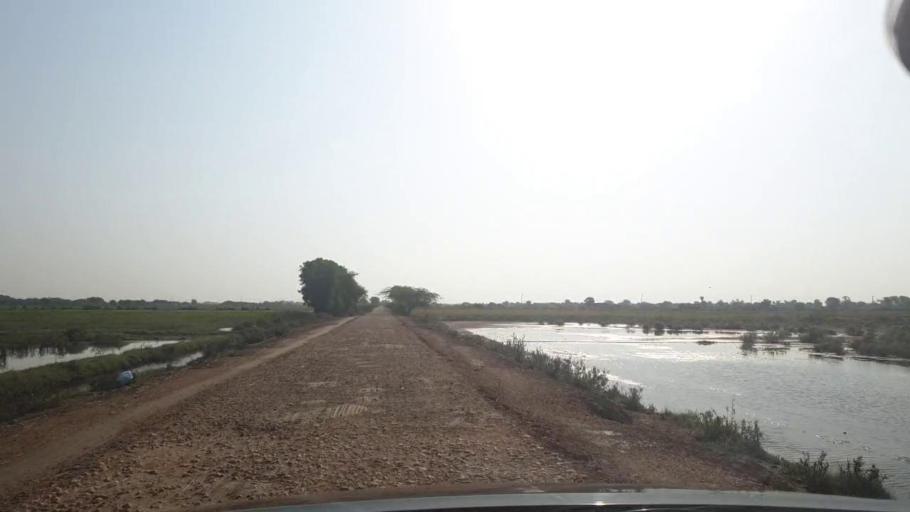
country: PK
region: Sindh
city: Tando Bago
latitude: 24.6510
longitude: 69.1441
